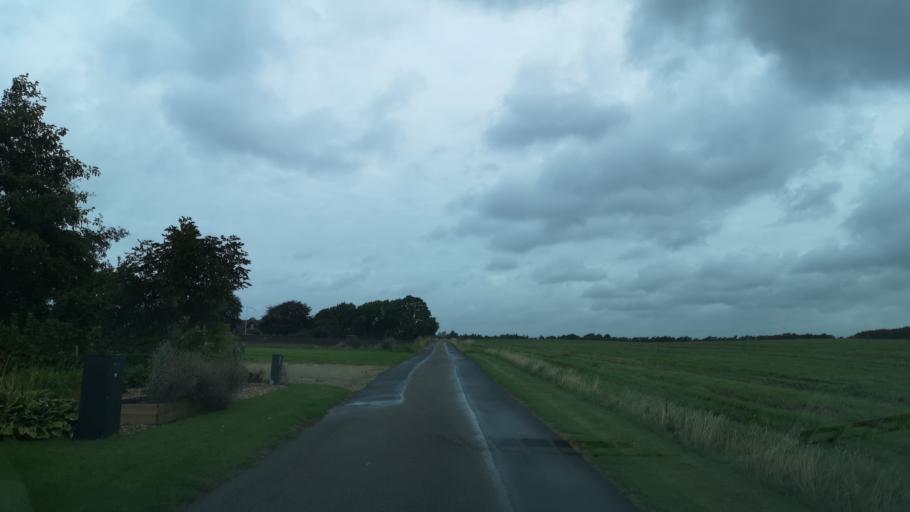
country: DK
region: Central Jutland
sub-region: Ringkobing-Skjern Kommune
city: Skjern
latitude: 55.9732
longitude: 8.5451
